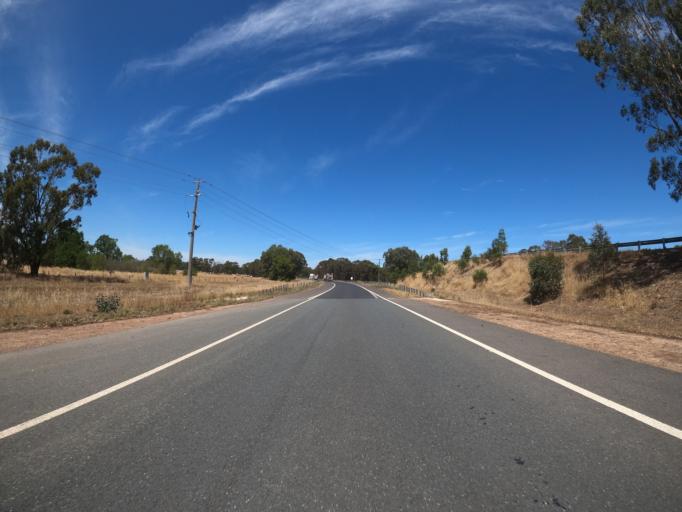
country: AU
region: Victoria
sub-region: Benalla
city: Benalla
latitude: -36.5211
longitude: 146.0642
